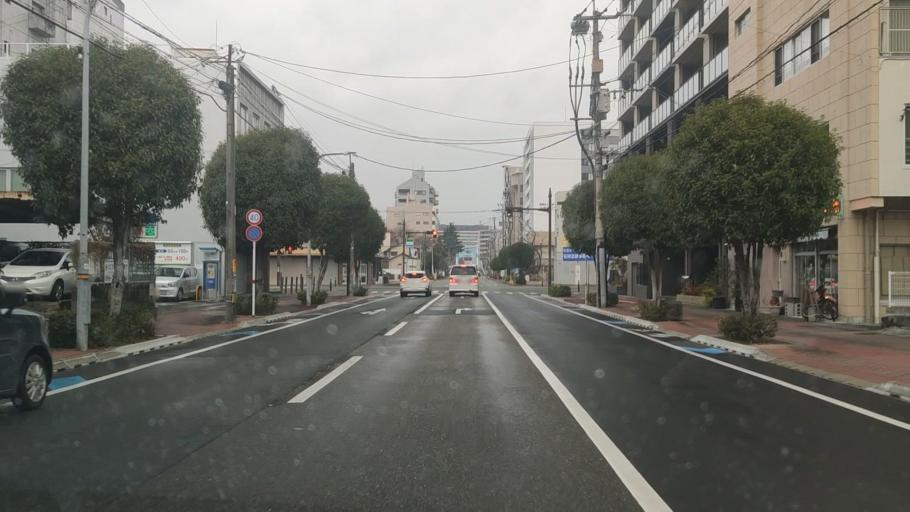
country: JP
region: Kumamoto
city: Kumamoto
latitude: 32.7964
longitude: 130.7154
